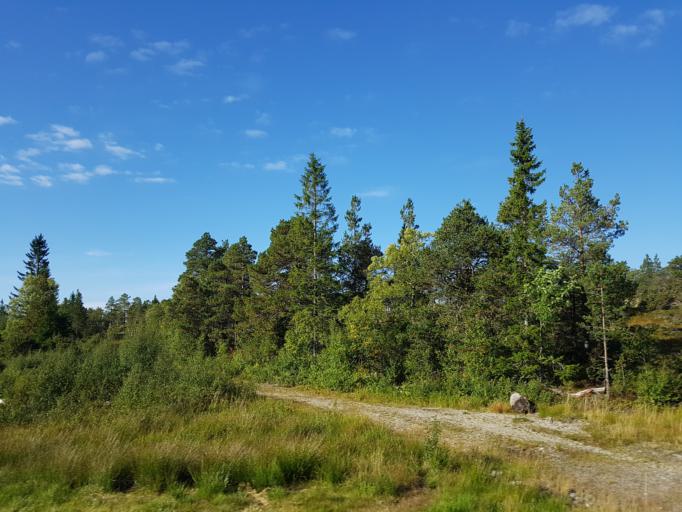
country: NO
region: Sor-Trondelag
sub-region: Trondheim
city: Trondheim
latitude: 63.6398
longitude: 10.2709
